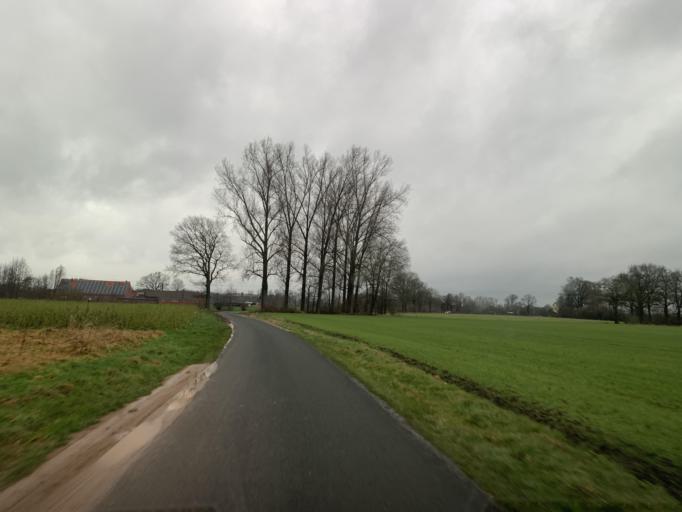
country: DE
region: North Rhine-Westphalia
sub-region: Regierungsbezirk Munster
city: Nordwalde
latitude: 52.0912
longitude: 7.5135
